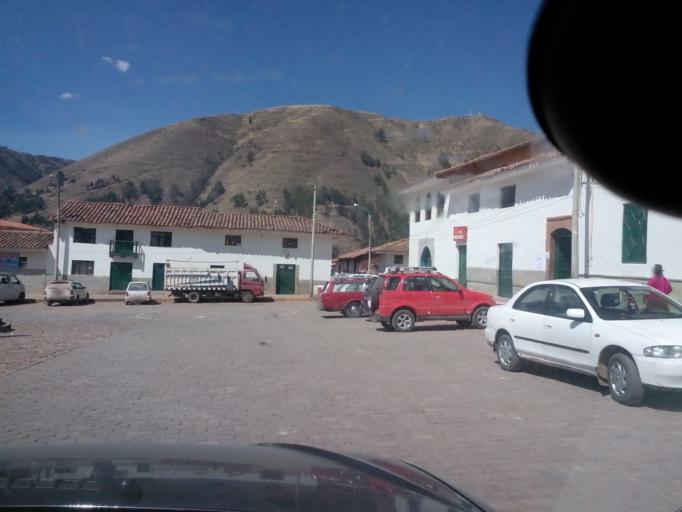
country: PE
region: Cusco
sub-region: Provincia de Anta
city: Huarocondo
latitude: -13.4156
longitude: -72.2077
